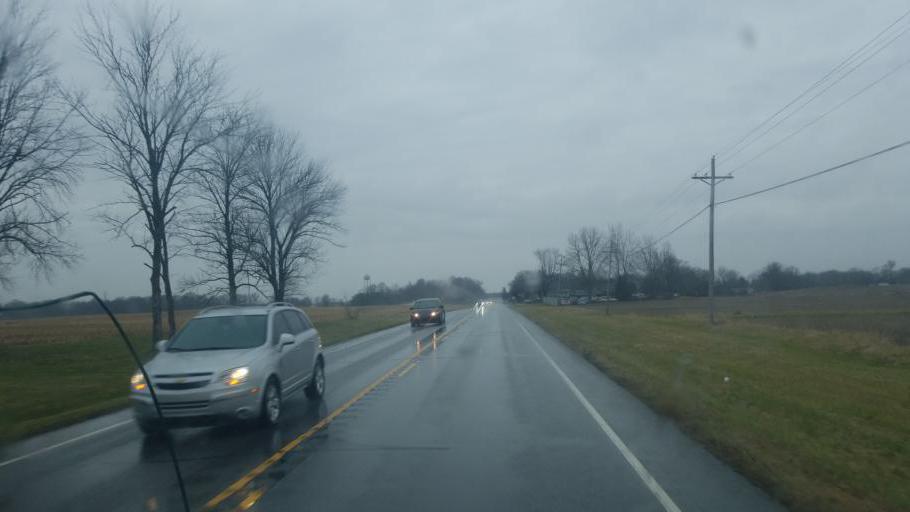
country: US
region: Indiana
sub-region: Bartholomew County
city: Columbus
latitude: 39.1880
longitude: -85.8514
